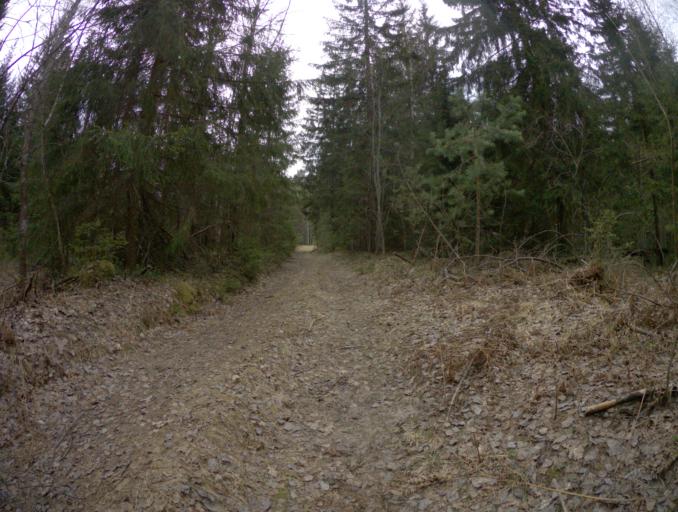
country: RU
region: Vladimir
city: Raduzhnyy
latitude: 55.9386
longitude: 40.2624
